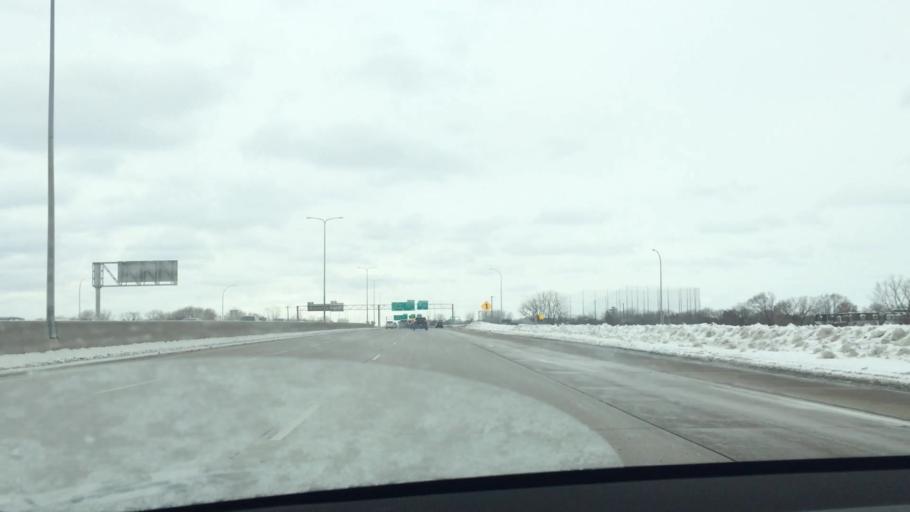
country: US
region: Minnesota
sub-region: Anoka County
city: Fridley
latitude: 45.0693
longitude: -93.2741
